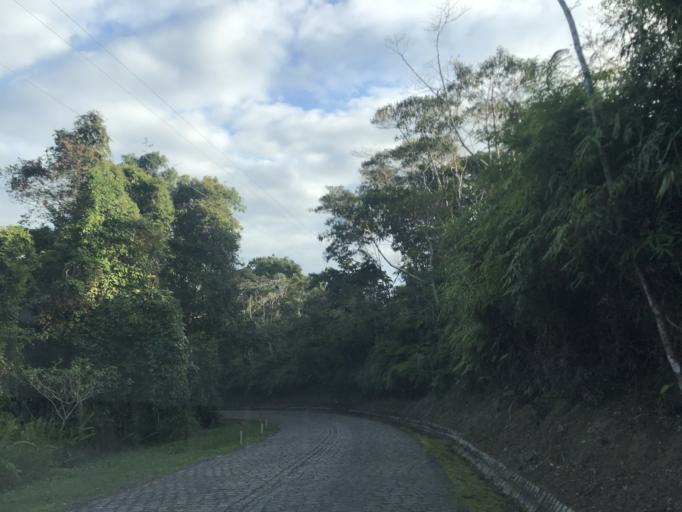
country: BR
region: Bahia
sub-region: Gandu
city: Gandu
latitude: -13.9022
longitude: -39.4614
